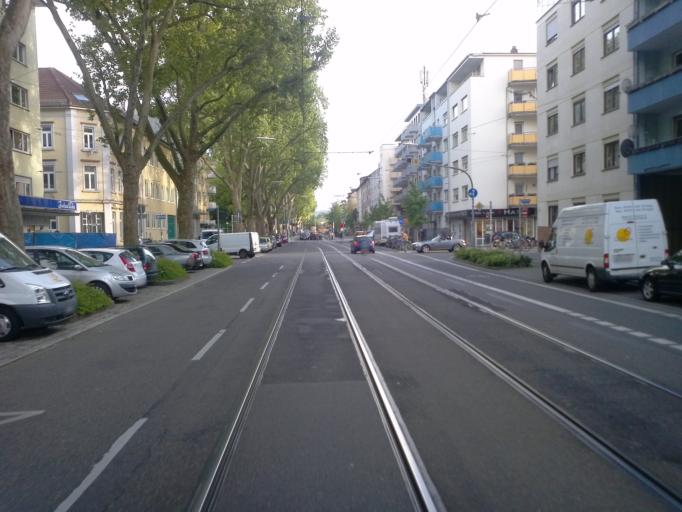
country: DE
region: Baden-Wuerttemberg
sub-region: Karlsruhe Region
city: Karlsruhe
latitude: 49.0018
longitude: 8.4106
